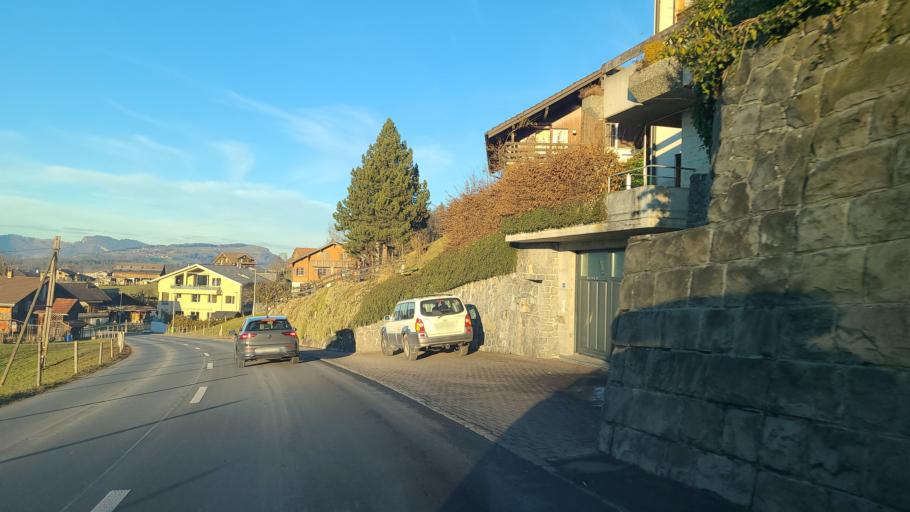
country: CH
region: Obwalden
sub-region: Obwalden
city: Kerns
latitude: 46.8958
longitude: 8.2795
